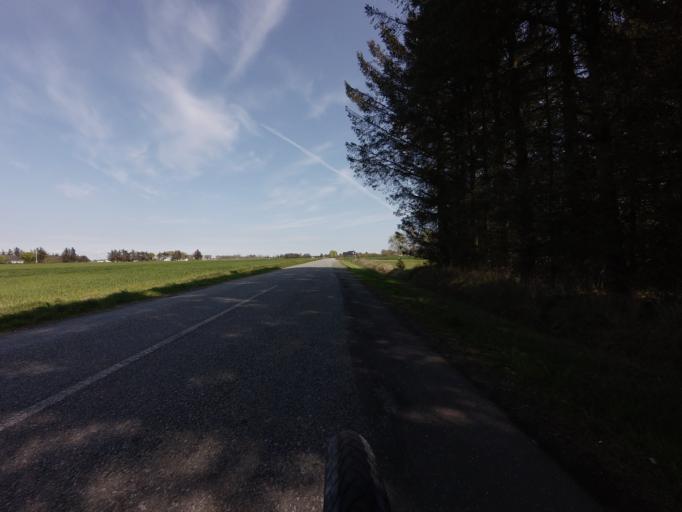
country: DK
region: North Denmark
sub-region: Jammerbugt Kommune
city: Pandrup
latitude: 57.2256
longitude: 9.6514
